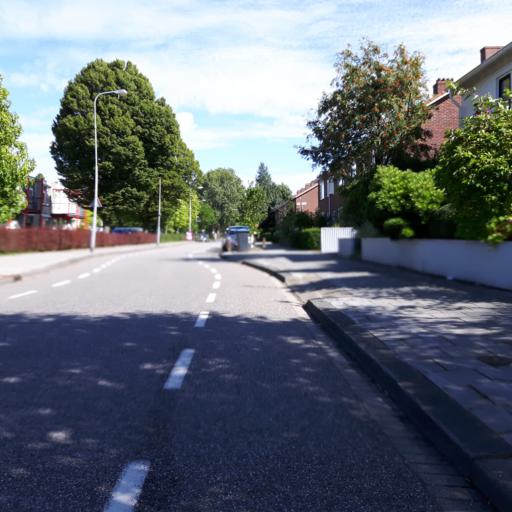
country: NL
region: Zeeland
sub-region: Gemeente Goes
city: Goes
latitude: 51.5039
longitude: 3.9044
